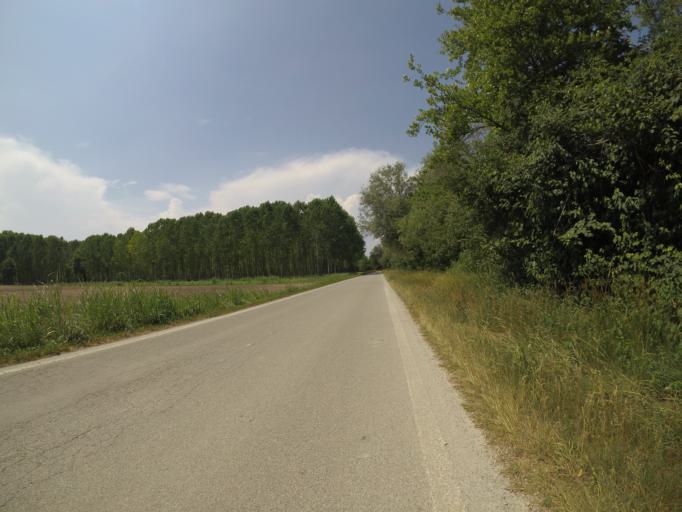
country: IT
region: Friuli Venezia Giulia
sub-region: Provincia di Udine
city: Rivignano
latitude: 45.8959
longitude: 13.0462
